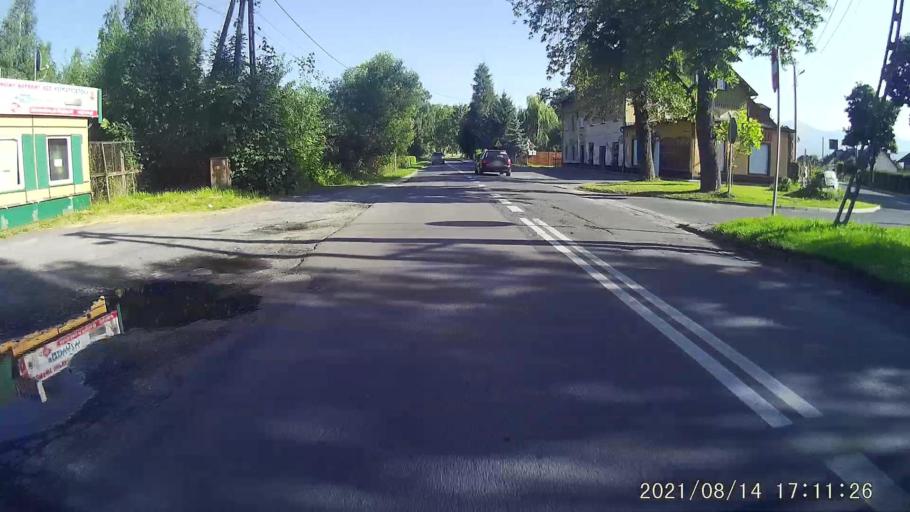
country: PL
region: Lower Silesian Voivodeship
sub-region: Powiat jeleniogorski
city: Myslakowice
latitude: 50.8347
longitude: 15.7891
